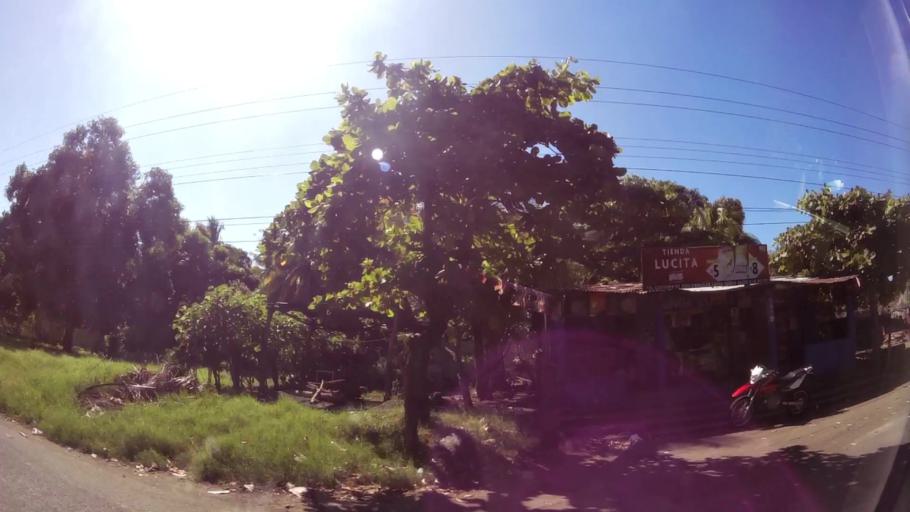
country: GT
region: Escuintla
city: Iztapa
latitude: 13.9247
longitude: -90.5847
